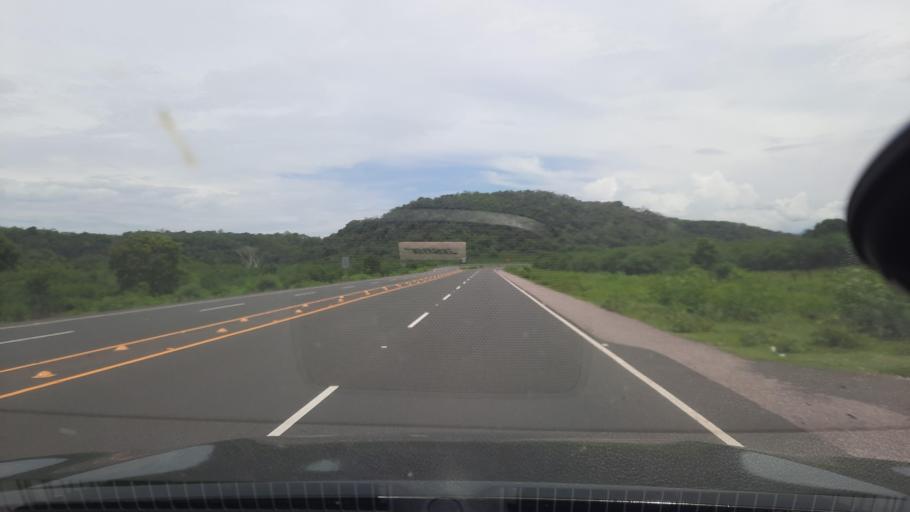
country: HN
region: Valle
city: Aramecina
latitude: 13.7279
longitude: -87.7126
